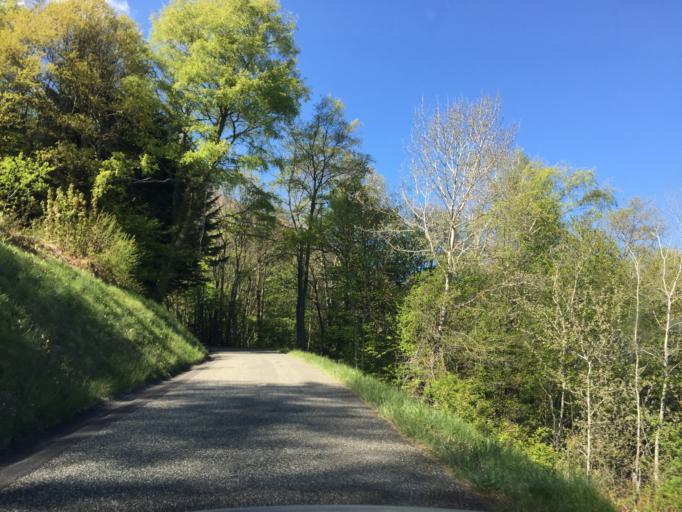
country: FR
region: Rhone-Alpes
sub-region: Departement de la Savoie
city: La Motte-Servolex
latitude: 45.5888
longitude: 5.8293
